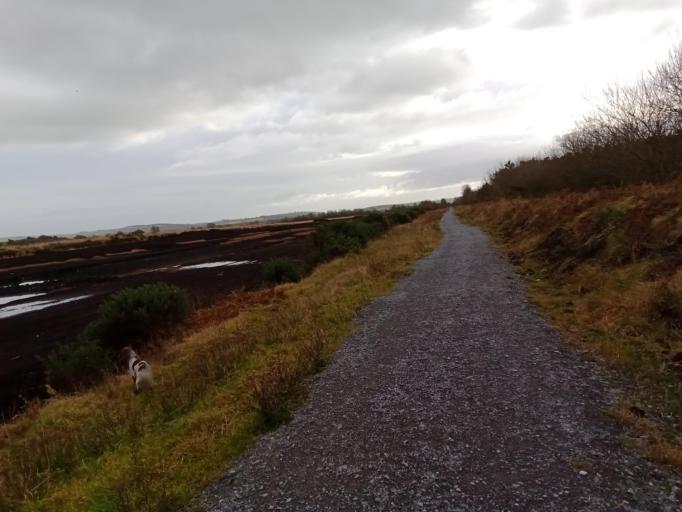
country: IE
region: Munster
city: Thurles
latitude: 52.5973
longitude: -7.7466
